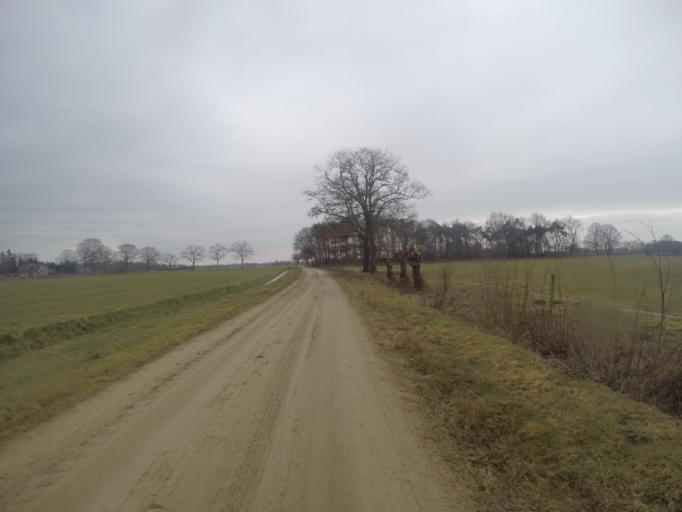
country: NL
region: Gelderland
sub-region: Gemeente Bronckhorst
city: Zelhem
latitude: 52.0315
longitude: 6.3445
